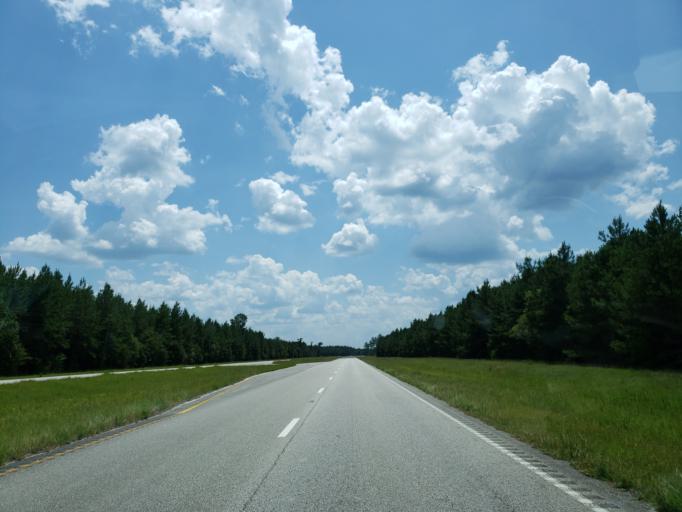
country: US
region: Mississippi
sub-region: Greene County
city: Leakesville
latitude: 31.2922
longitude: -88.5014
